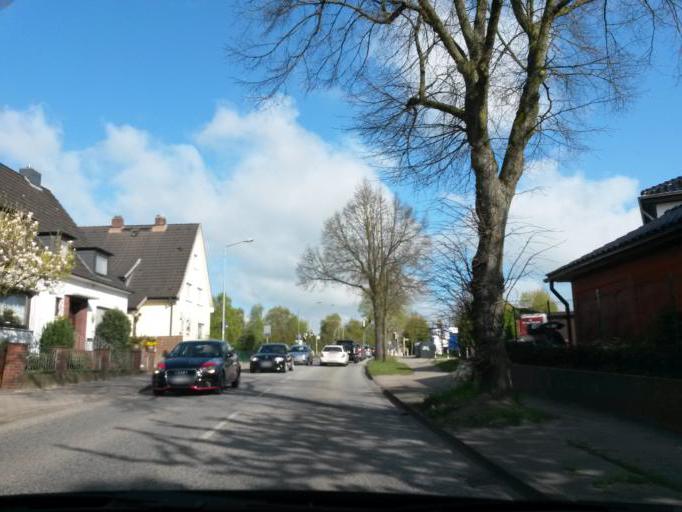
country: DE
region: Schleswig-Holstein
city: Wedel
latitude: 53.5873
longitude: 9.6910
